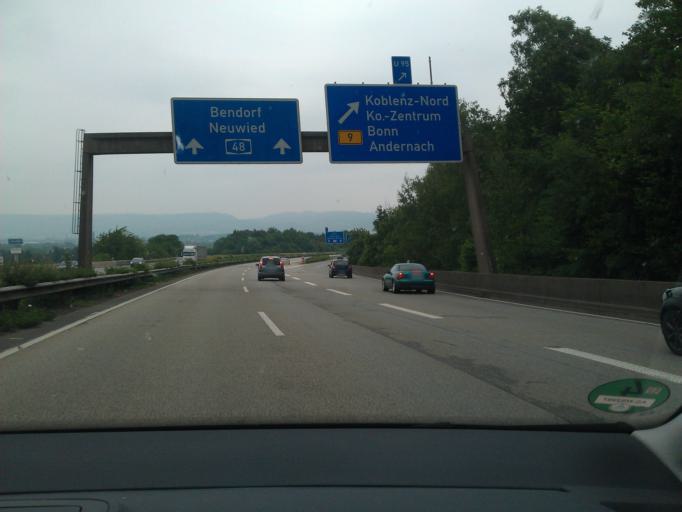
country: DE
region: Rheinland-Pfalz
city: Kaltenengers
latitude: 50.3880
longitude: 7.5399
